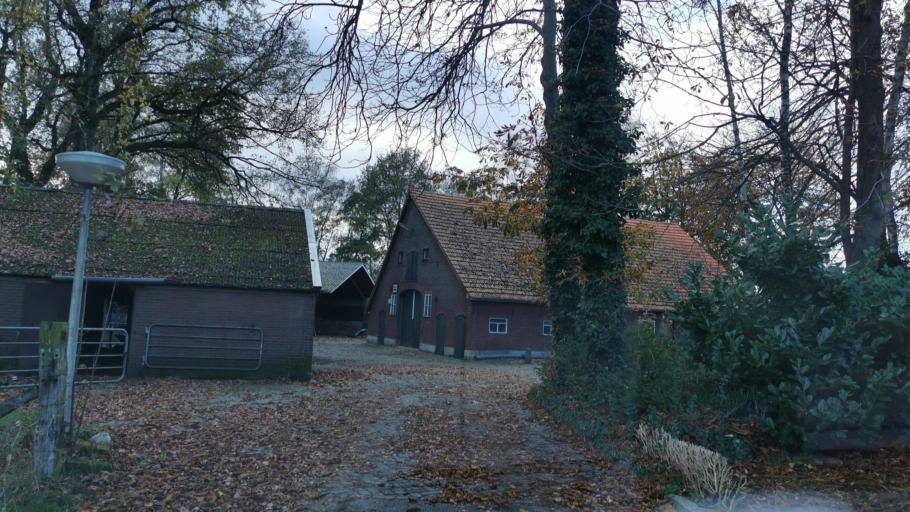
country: DE
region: North Rhine-Westphalia
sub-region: Regierungsbezirk Munster
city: Gronau
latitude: 52.2305
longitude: 7.0378
